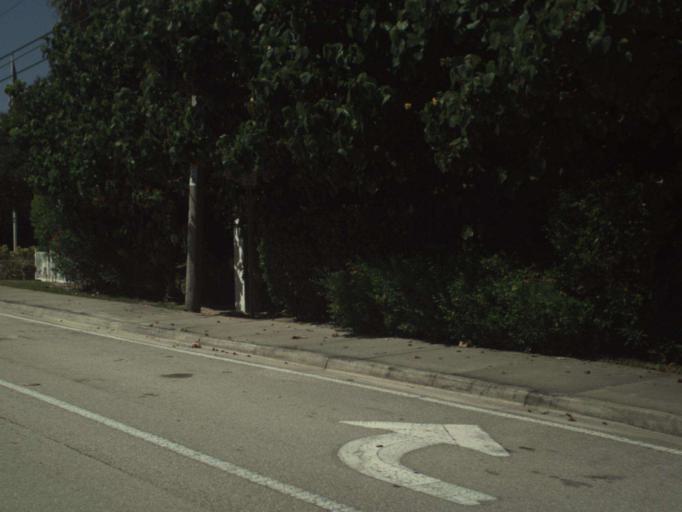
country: US
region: Florida
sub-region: Indian River County
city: Wabasso Beach
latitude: 27.7552
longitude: -80.3935
